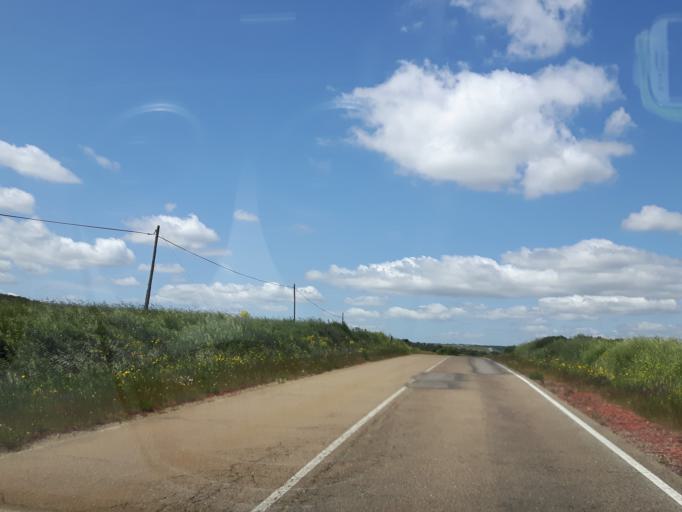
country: ES
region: Castille and Leon
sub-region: Provincia de Salamanca
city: Villar de Ciervo
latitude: 40.7256
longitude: -6.7582
